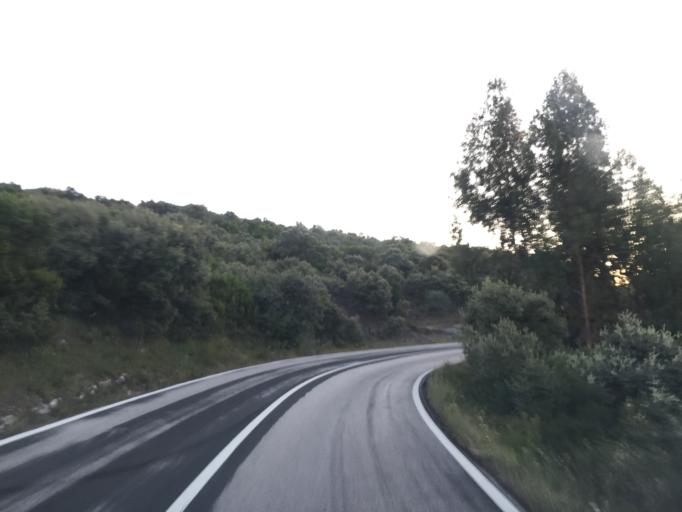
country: PT
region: Santarem
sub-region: Ourem
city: Fatima
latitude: 39.6312
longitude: -8.6342
